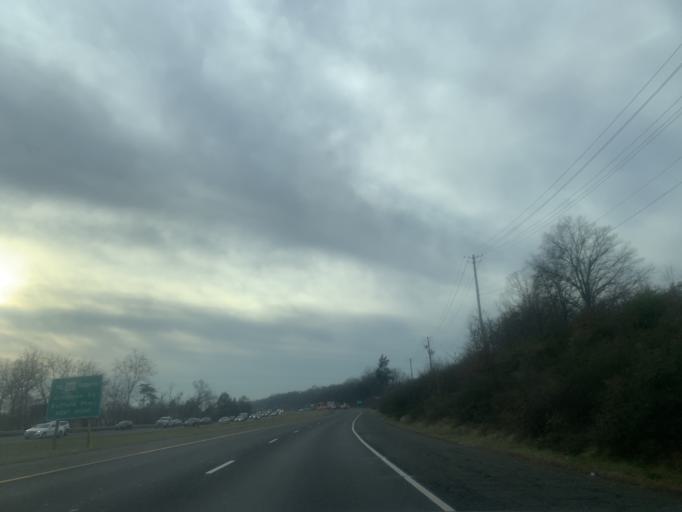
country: US
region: Maryland
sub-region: Prince George's County
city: Forestville
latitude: 38.8344
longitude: -76.8587
